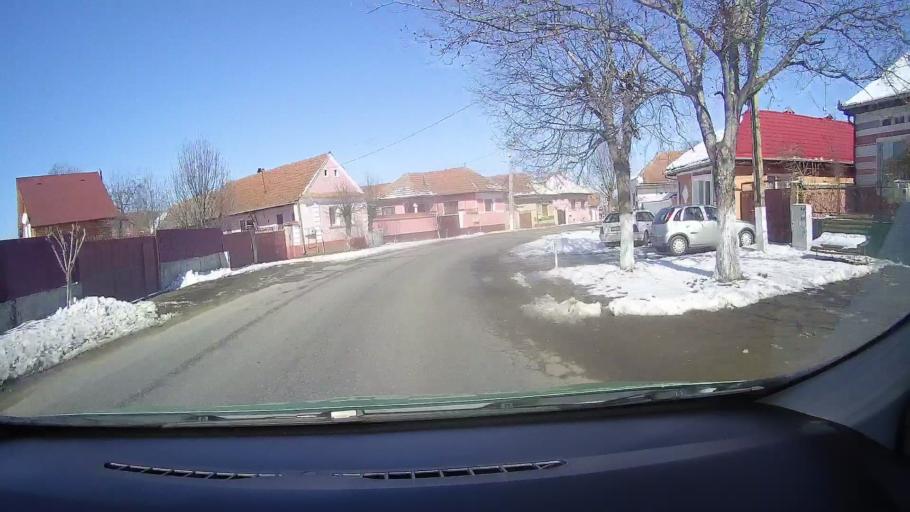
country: RO
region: Brasov
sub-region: Comuna Harseni
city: Harseni
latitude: 45.7855
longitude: 24.9996
